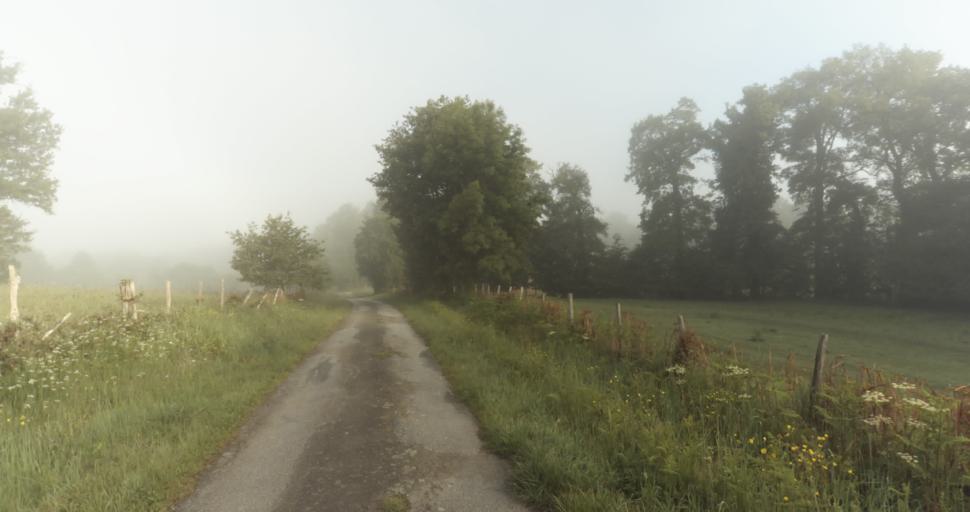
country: FR
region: Limousin
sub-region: Departement de la Haute-Vienne
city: Condat-sur-Vienne
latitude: 45.7863
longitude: 1.2804
